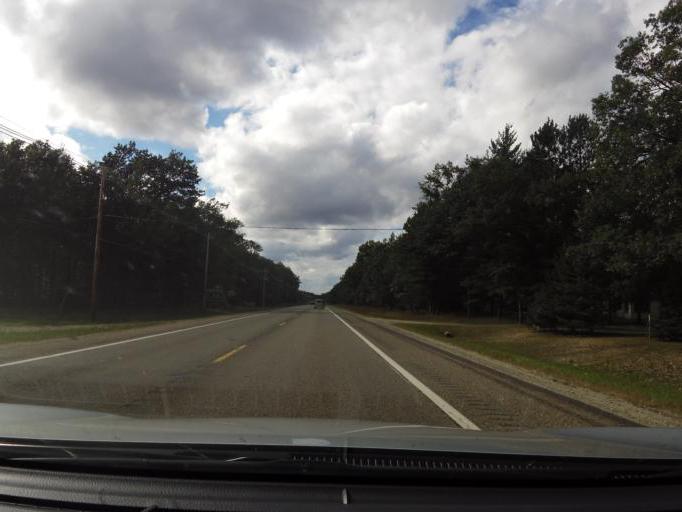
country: US
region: Michigan
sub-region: Roscommon County
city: Prudenville
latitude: 44.3055
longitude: -84.6210
